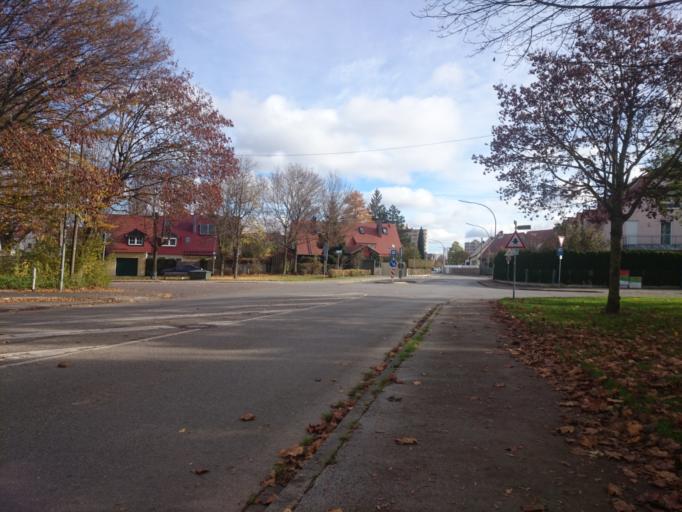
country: DE
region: Bavaria
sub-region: Swabia
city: Konigsbrunn
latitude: 48.3046
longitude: 10.8974
